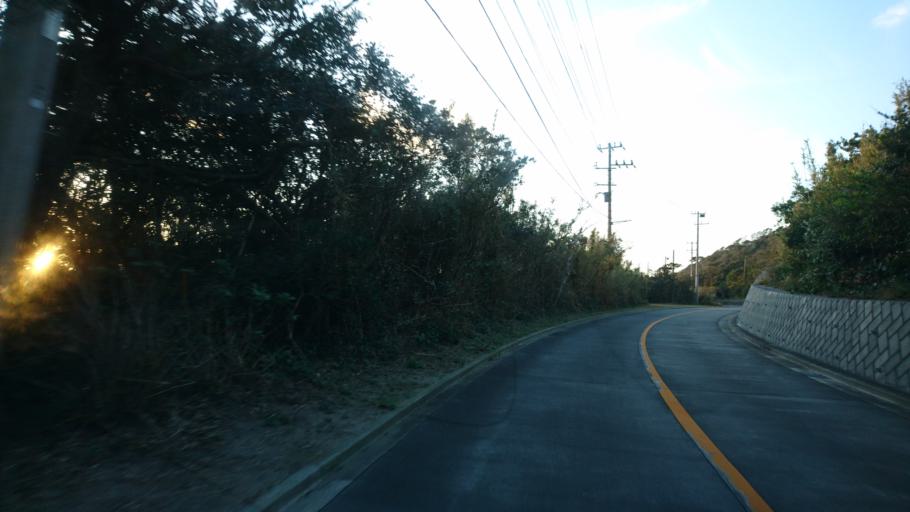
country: JP
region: Shizuoka
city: Shimoda
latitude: 34.3629
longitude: 139.2464
